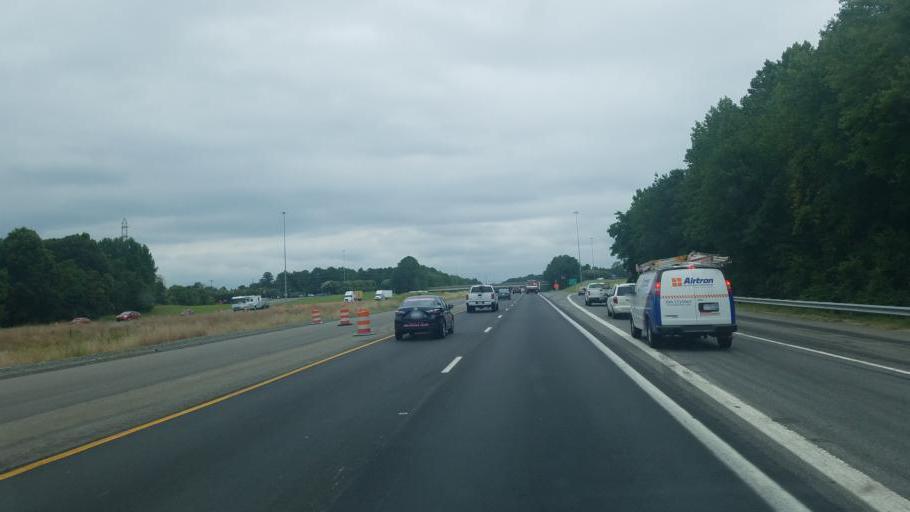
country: US
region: North Carolina
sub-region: Mecklenburg County
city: Huntersville
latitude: 35.4047
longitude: -80.8566
